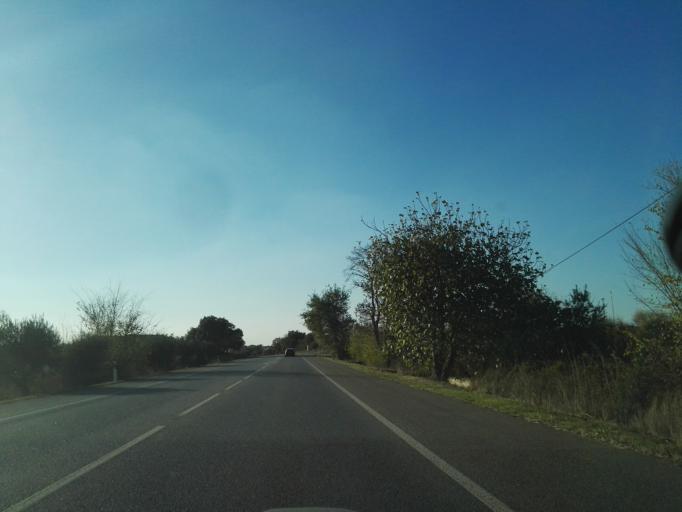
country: PT
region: Evora
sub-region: Estremoz
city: Estremoz
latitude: 38.8358
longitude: -7.5685
